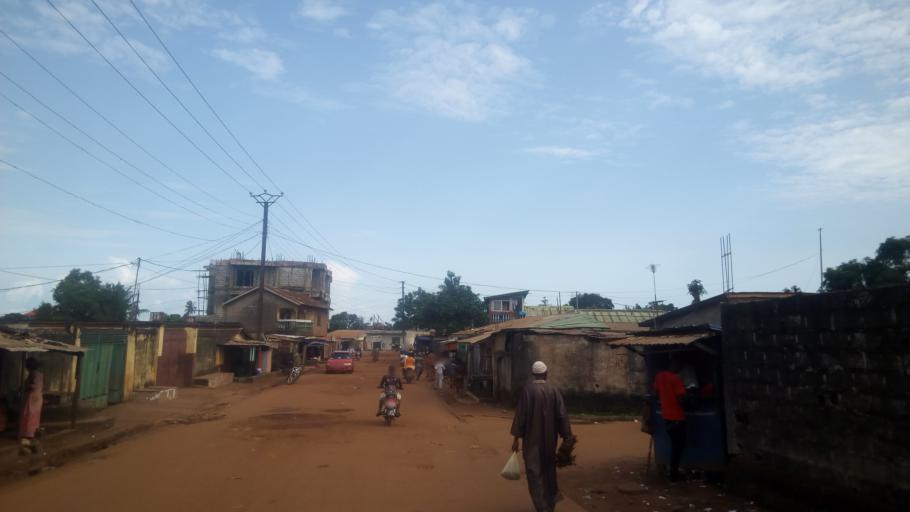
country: GN
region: Kindia
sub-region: Prefecture de Dubreka
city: Dubreka
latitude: 9.6540
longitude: -13.5348
